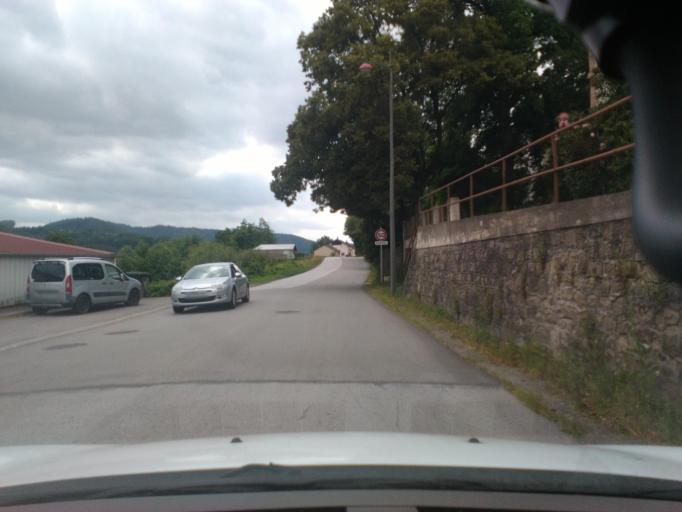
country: FR
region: Lorraine
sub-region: Departement des Vosges
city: Bruyeres
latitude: 48.1787
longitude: 6.6787
